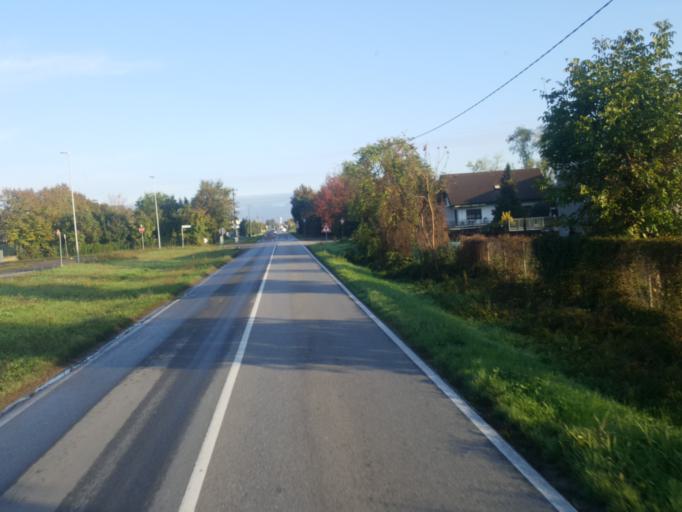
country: IT
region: Lombardy
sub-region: Provincia di Bergamo
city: Cologno al Serio
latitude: 45.5574
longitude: 9.7073
